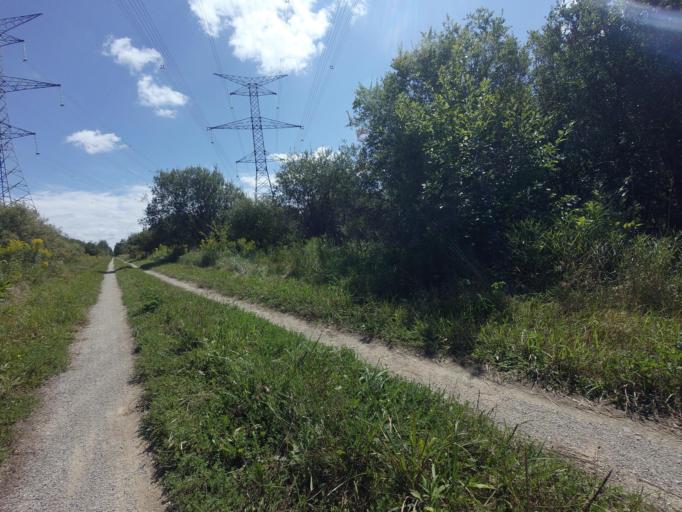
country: CA
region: Ontario
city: Orangeville
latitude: 43.7803
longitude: -80.2157
